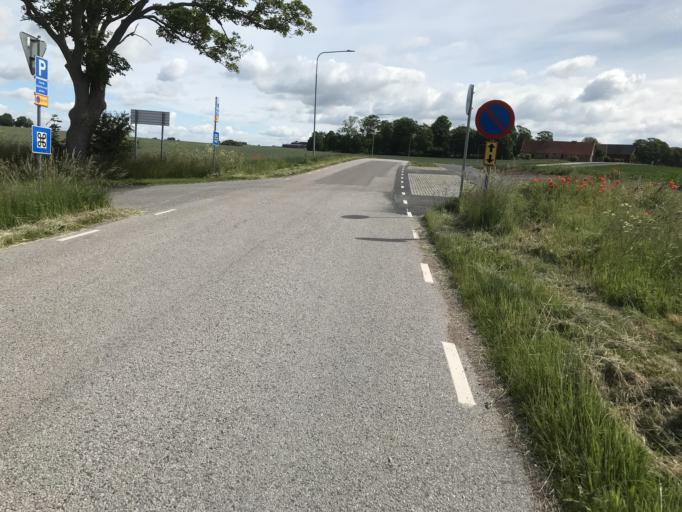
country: SE
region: Skane
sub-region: Helsingborg
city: Rydeback
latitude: 55.9438
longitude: 12.7720
